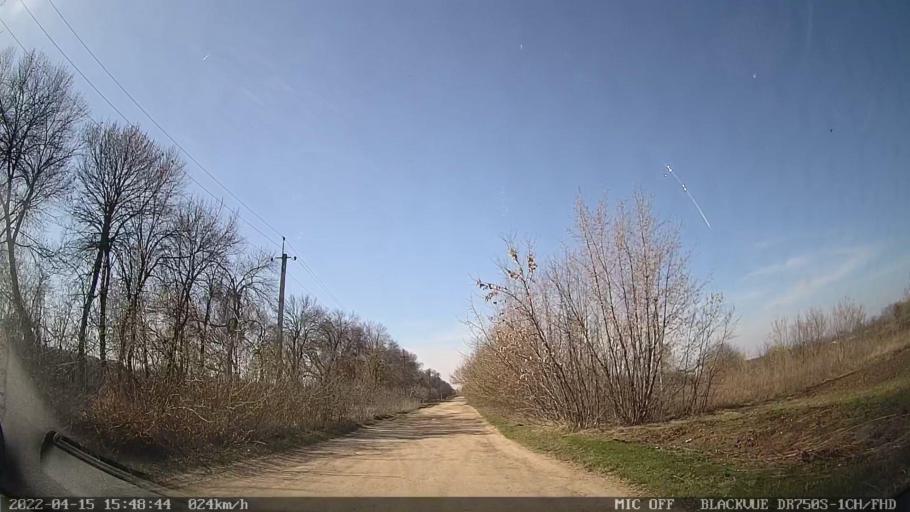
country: MD
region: Raionul Ocnita
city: Otaci
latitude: 48.3878
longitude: 27.9058
